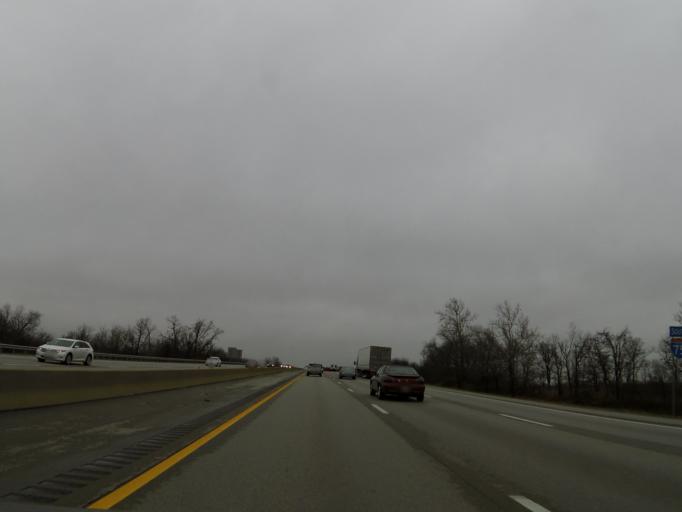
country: US
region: Kentucky
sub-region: Scott County
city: Georgetown
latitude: 38.2681
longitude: -84.5547
